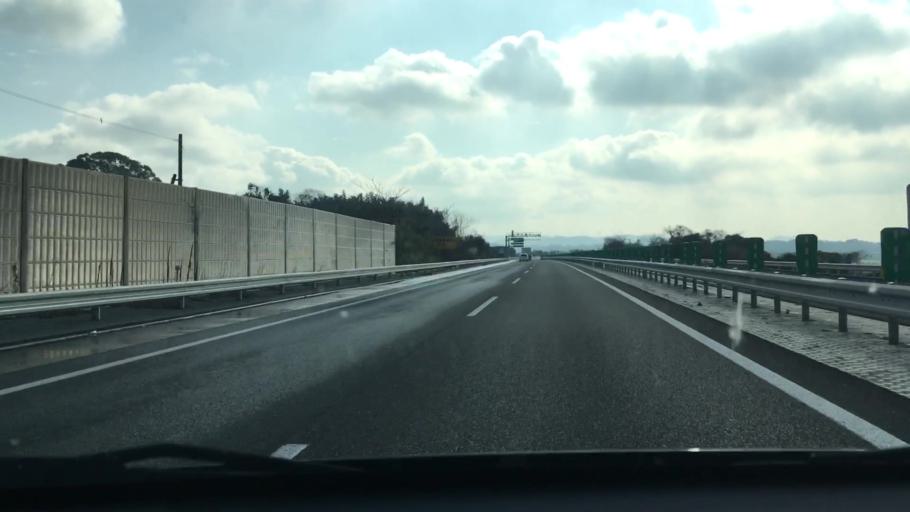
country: JP
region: Kumamoto
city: Uto
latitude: 32.7231
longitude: 130.7712
